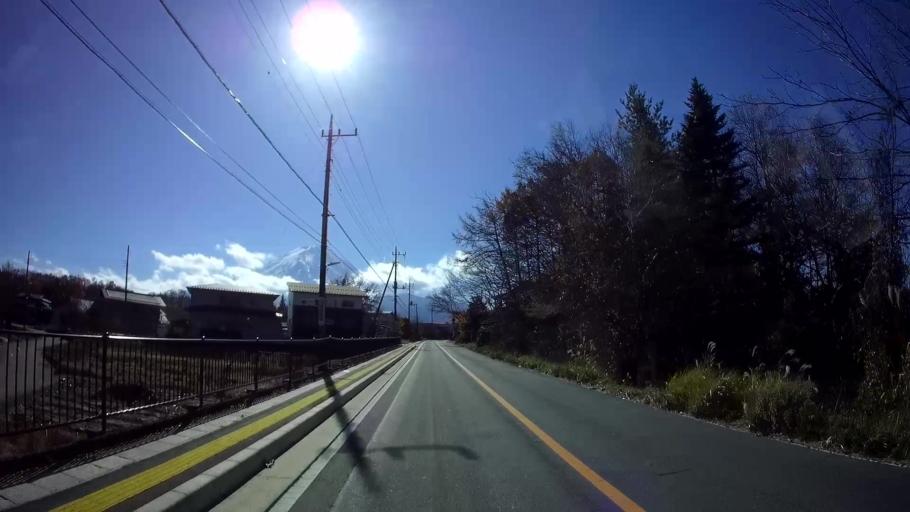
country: JP
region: Yamanashi
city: Fujikawaguchiko
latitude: 35.4880
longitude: 138.7273
